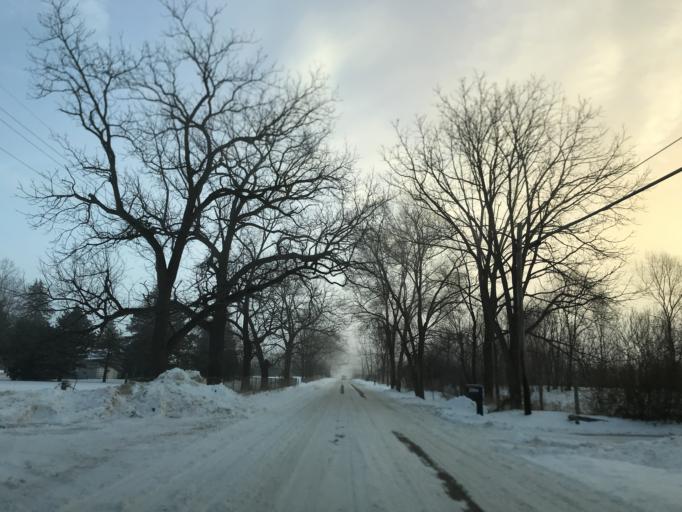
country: US
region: Michigan
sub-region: Oakland County
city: Wixom
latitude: 42.4925
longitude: -83.5705
